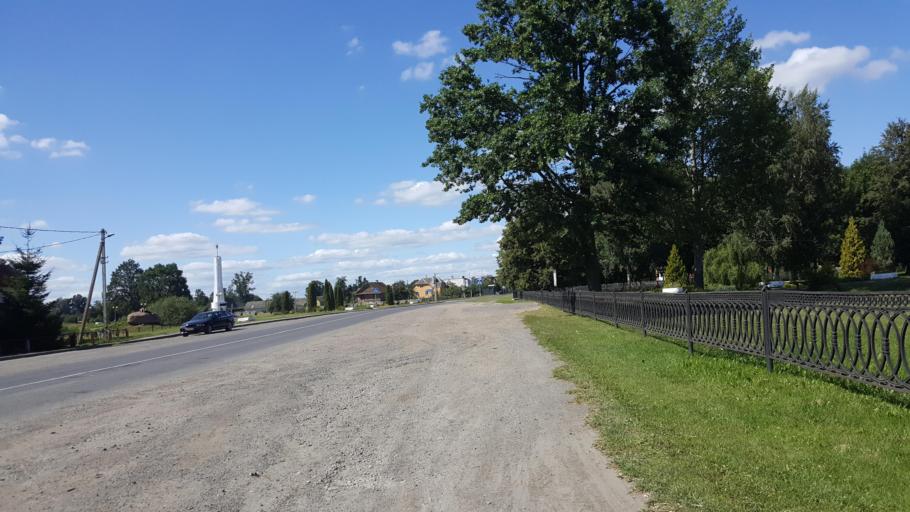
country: BY
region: Brest
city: Kobryn
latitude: 52.2996
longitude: 24.2763
